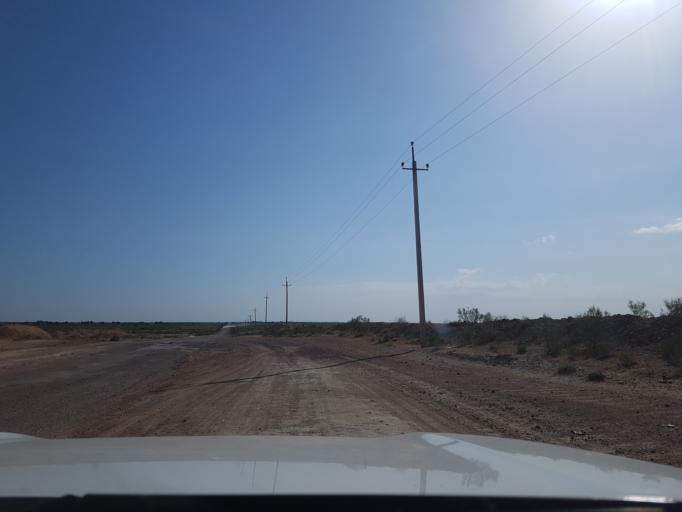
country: TM
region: Dasoguz
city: Koeneuergench
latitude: 42.0282
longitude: 58.7984
